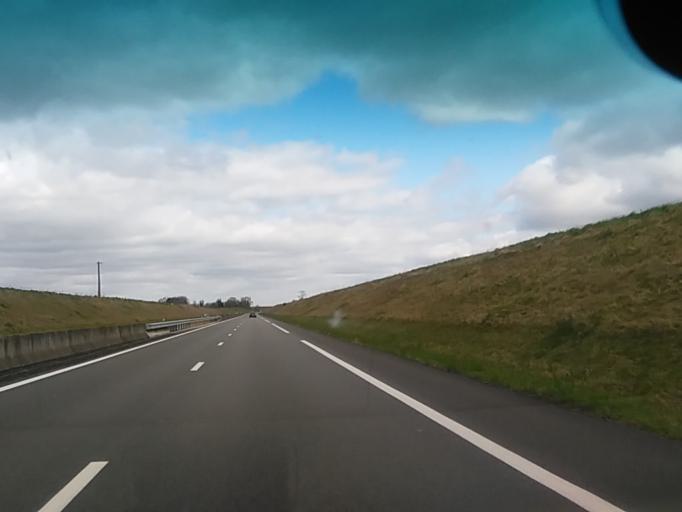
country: FR
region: Haute-Normandie
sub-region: Departement de l'Eure
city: Thiberville
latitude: 49.1028
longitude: 0.5079
